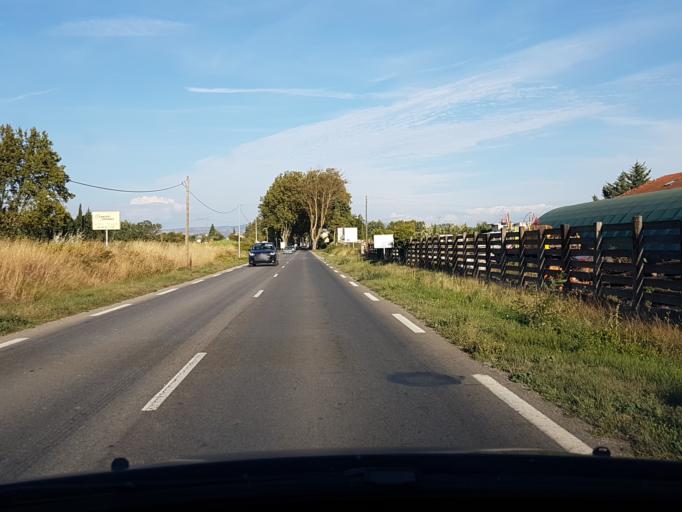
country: FR
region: Provence-Alpes-Cote d'Azur
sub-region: Departement des Bouches-du-Rhone
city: Molleges
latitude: 43.7874
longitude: 4.9476
